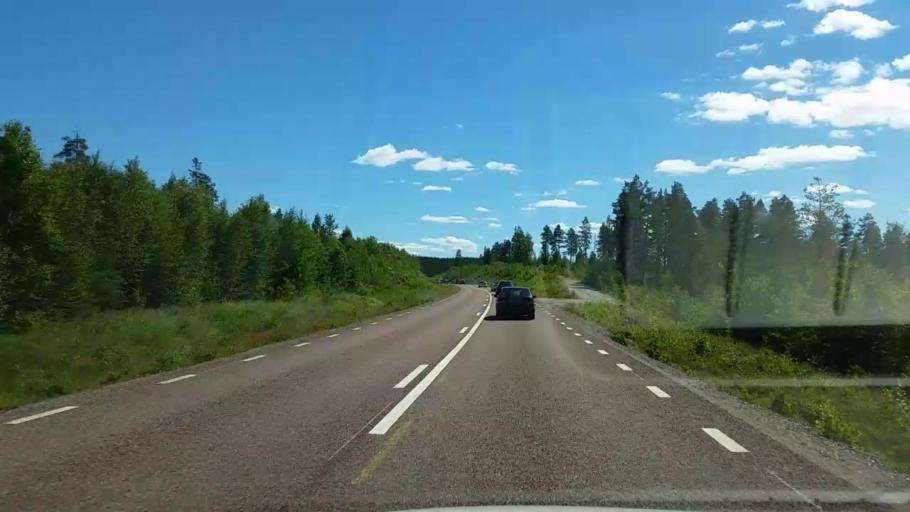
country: SE
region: Gaevleborg
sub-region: Ovanakers Kommun
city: Edsbyn
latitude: 61.2366
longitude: 15.8814
